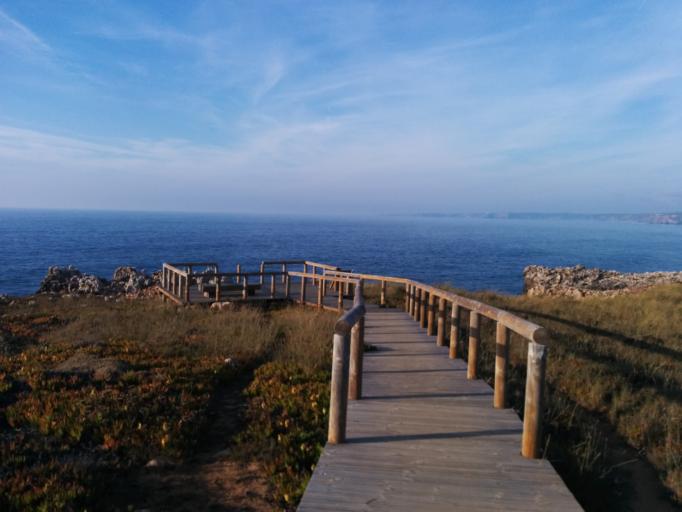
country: PT
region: Faro
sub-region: Vila do Bispo
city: Vila do Bispo
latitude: 37.1972
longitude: -8.9126
